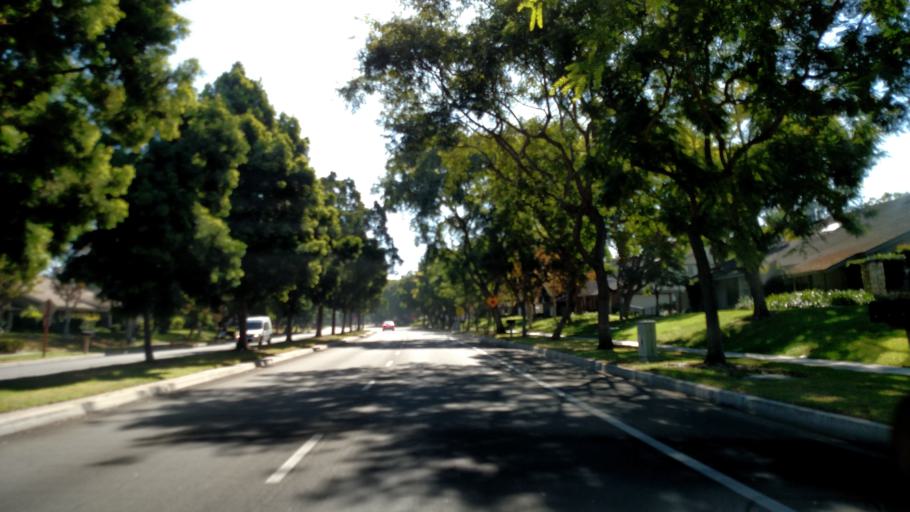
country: US
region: California
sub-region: Orange County
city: Irvine
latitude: 33.6835
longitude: -117.7899
